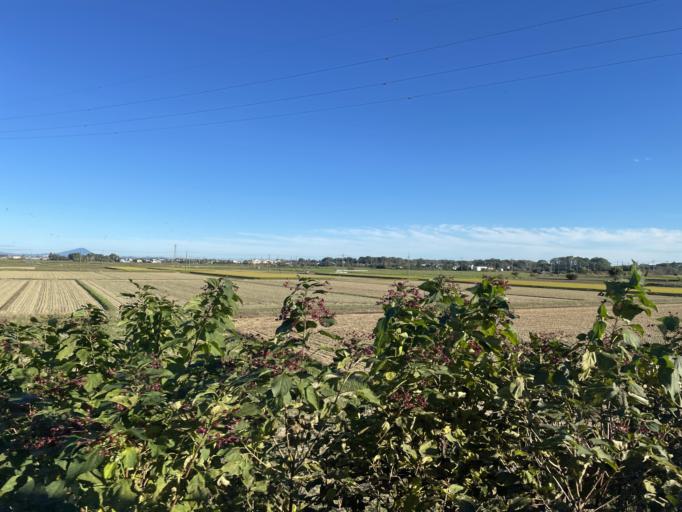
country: JP
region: Tochigi
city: Tochigi
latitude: 36.3211
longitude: 139.6896
